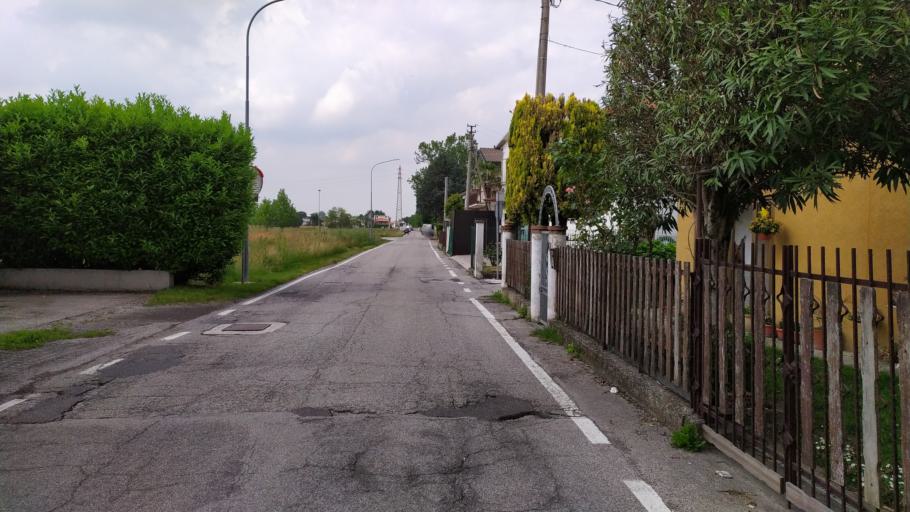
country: IT
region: Veneto
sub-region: Provincia di Padova
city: Vigodarzere
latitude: 45.4521
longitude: 11.8939
